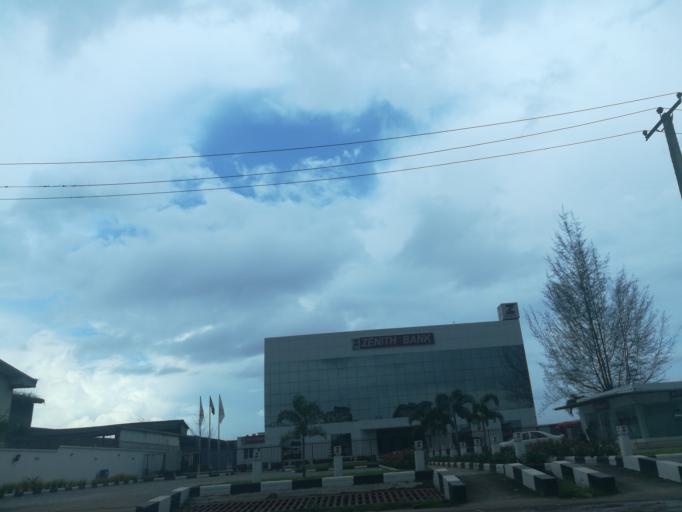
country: NG
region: Lagos
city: Agege
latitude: 6.6133
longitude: 3.3357
